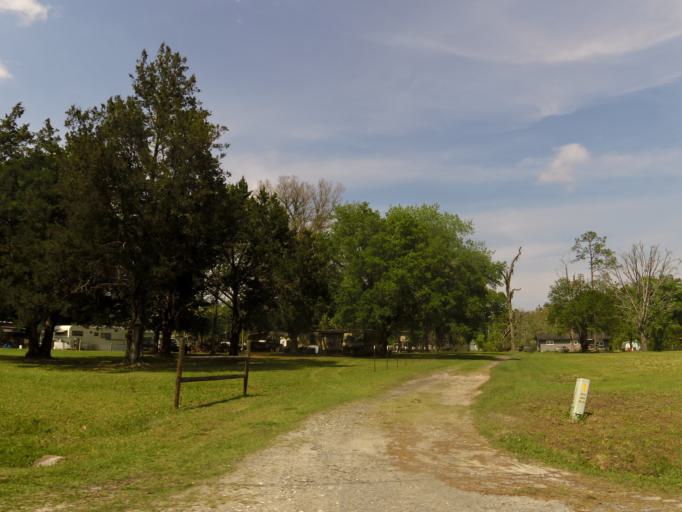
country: US
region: Georgia
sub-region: Camden County
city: Kingsland
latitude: 30.8042
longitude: -81.7443
